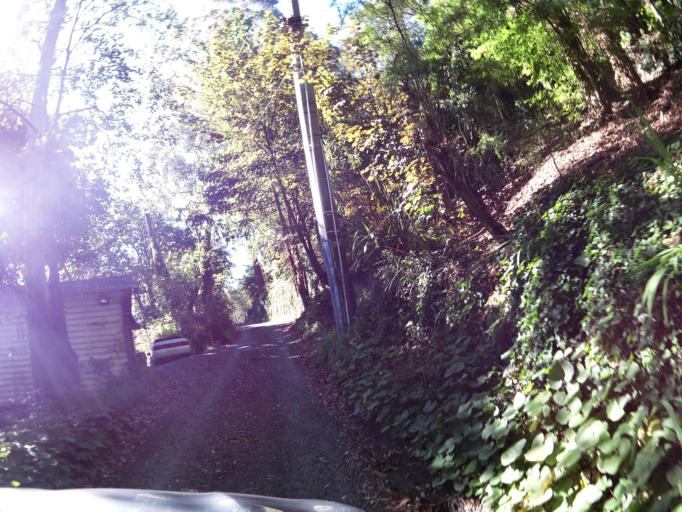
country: AU
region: Victoria
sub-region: Yarra Ranges
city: Ferny Creek
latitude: -37.8885
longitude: 145.3344
